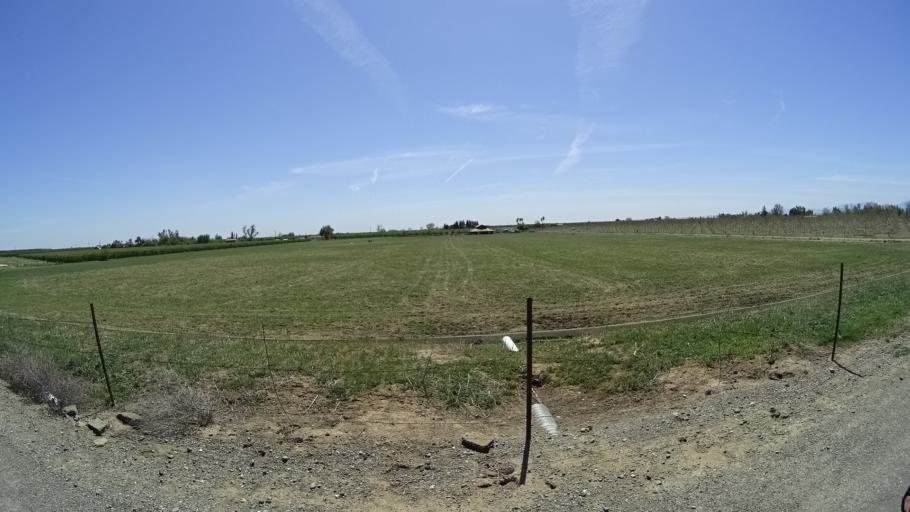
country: US
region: California
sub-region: Glenn County
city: Hamilton City
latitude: 39.7324
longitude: -122.0940
